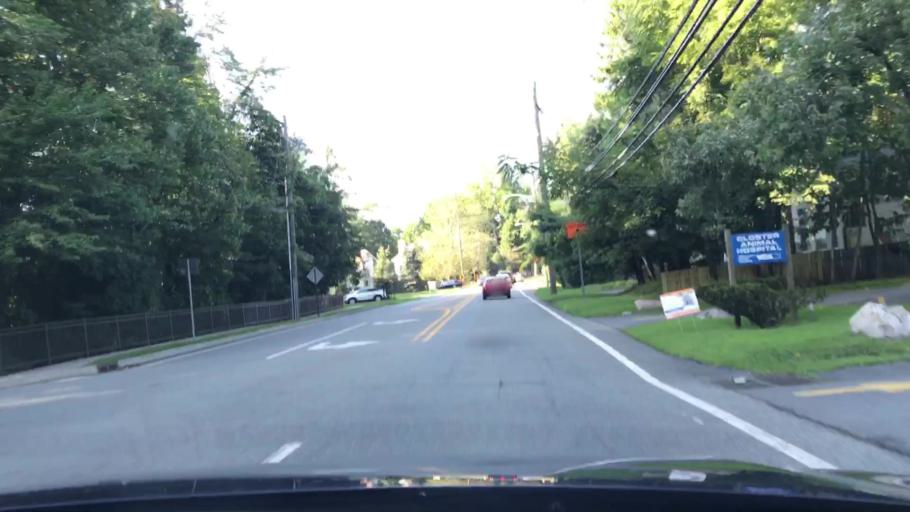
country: US
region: New Jersey
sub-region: Bergen County
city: Closter
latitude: 40.9784
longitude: -73.9444
